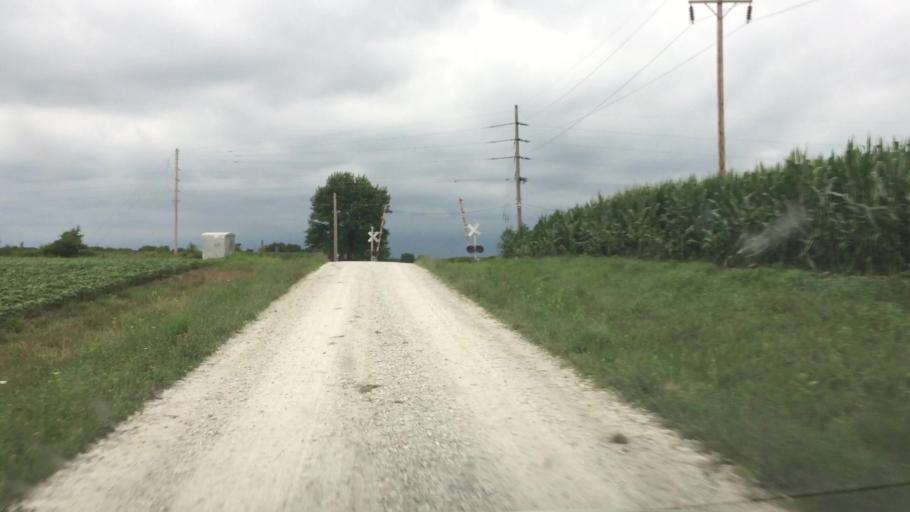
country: US
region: Illinois
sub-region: Adams County
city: Camp Point
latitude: 40.2155
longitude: -90.9588
